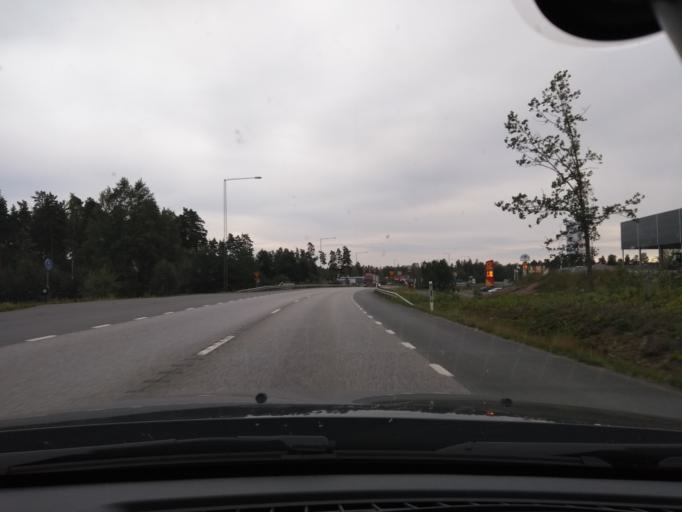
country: SE
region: Joenkoeping
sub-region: Eksjo Kommun
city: Eksjoe
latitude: 57.6511
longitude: 14.9533
